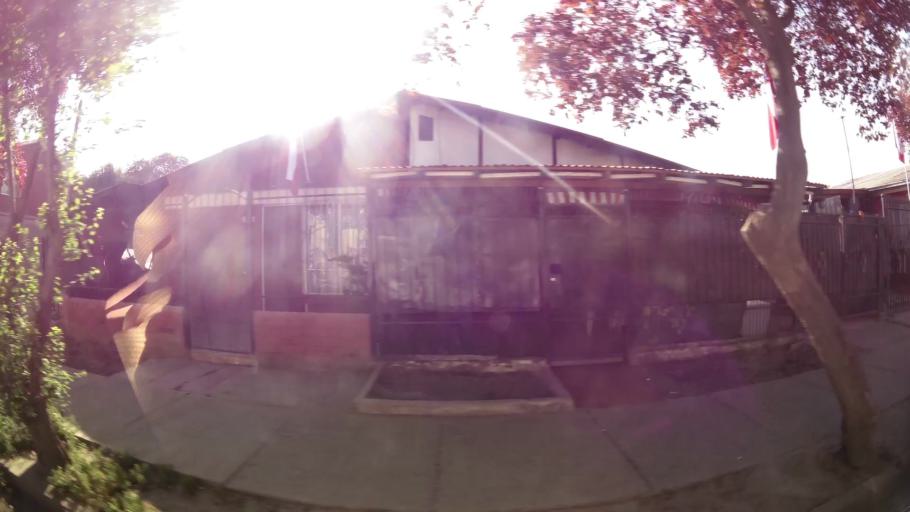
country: CL
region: Santiago Metropolitan
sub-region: Provincia de Santiago
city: Lo Prado
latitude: -33.4185
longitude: -70.7600
